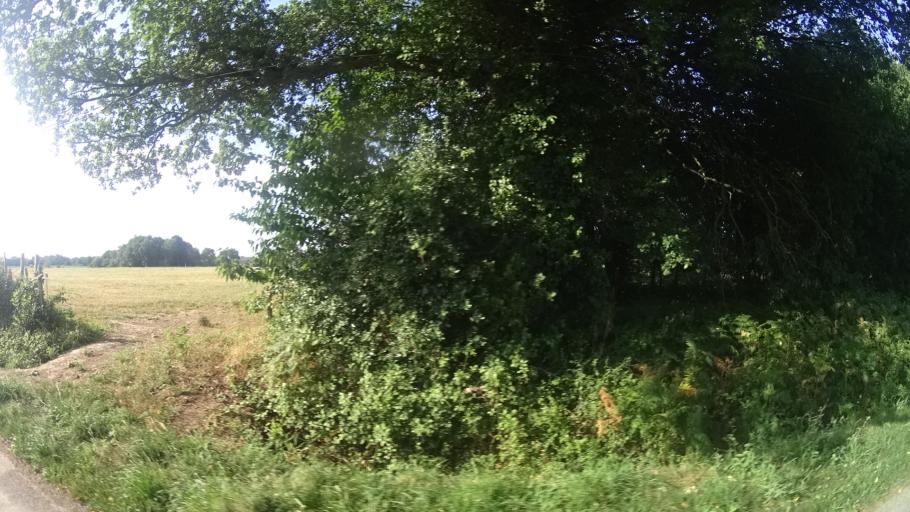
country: FR
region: Brittany
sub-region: Departement du Morbihan
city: Saint-Jean-la-Poterie
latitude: 47.6410
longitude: -2.1392
